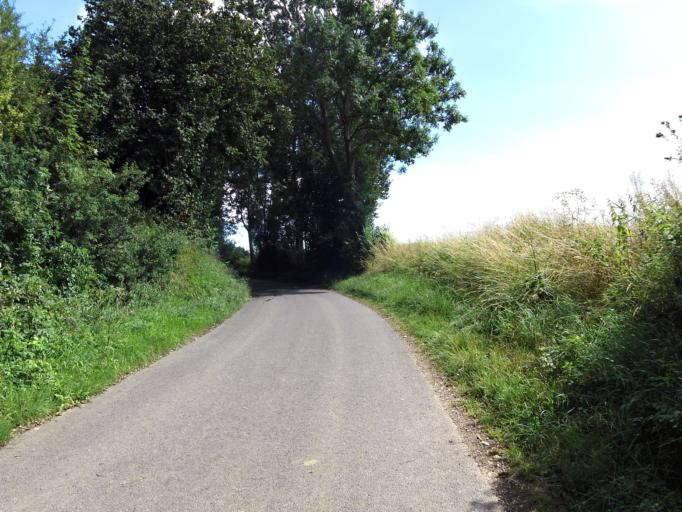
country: NL
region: Limburg
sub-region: Valkenburg aan de Geul
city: Schin op Geul
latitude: 50.8323
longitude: 5.9079
